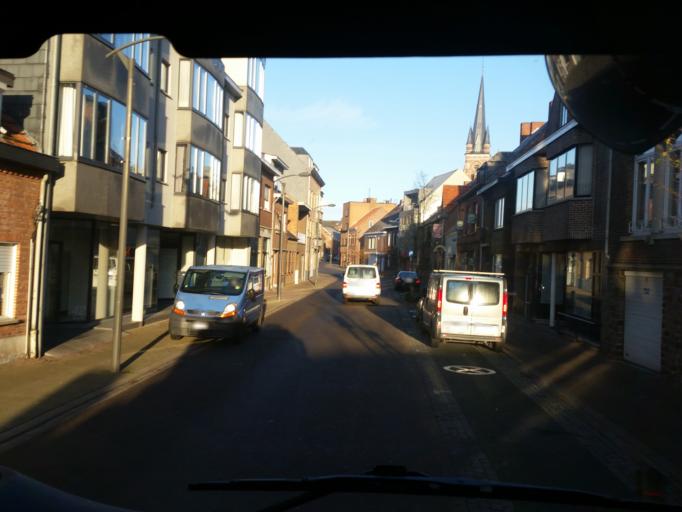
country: BE
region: Flanders
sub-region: Provincie Antwerpen
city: Arendonk
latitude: 51.3181
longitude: 5.0871
